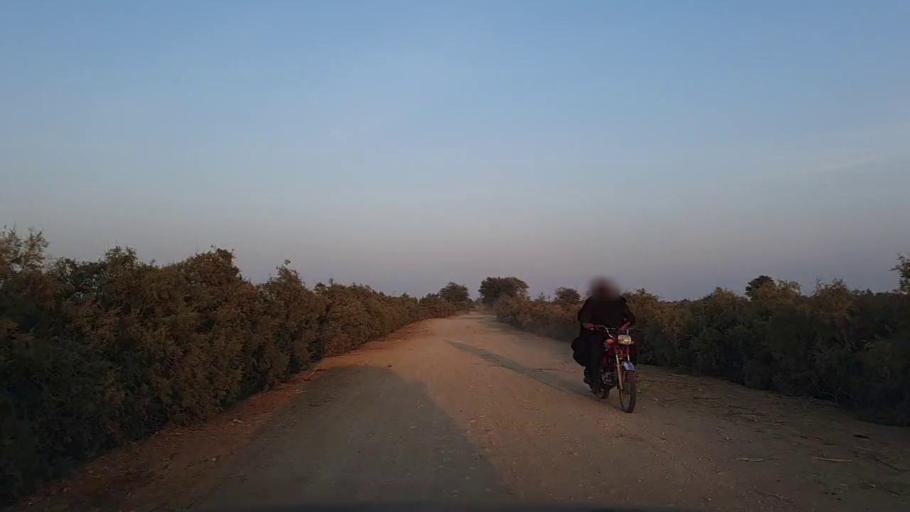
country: PK
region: Sindh
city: Tando Mittha Khan
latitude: 25.9780
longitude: 69.1091
